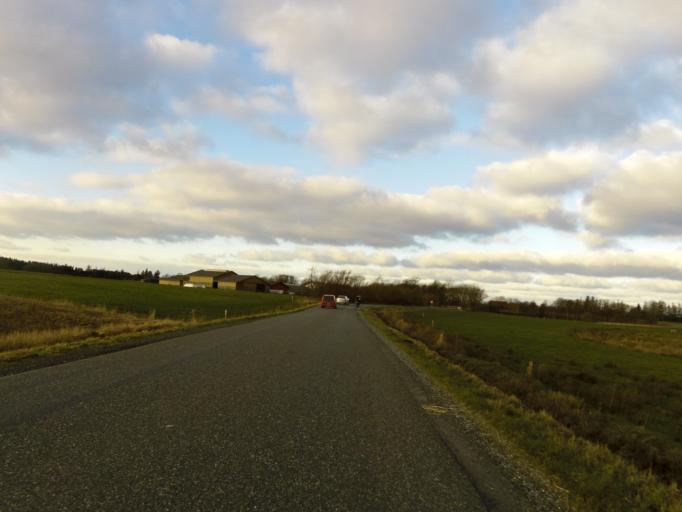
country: DK
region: South Denmark
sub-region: Esbjerg Kommune
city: Ribe
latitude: 55.3030
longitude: 8.8486
